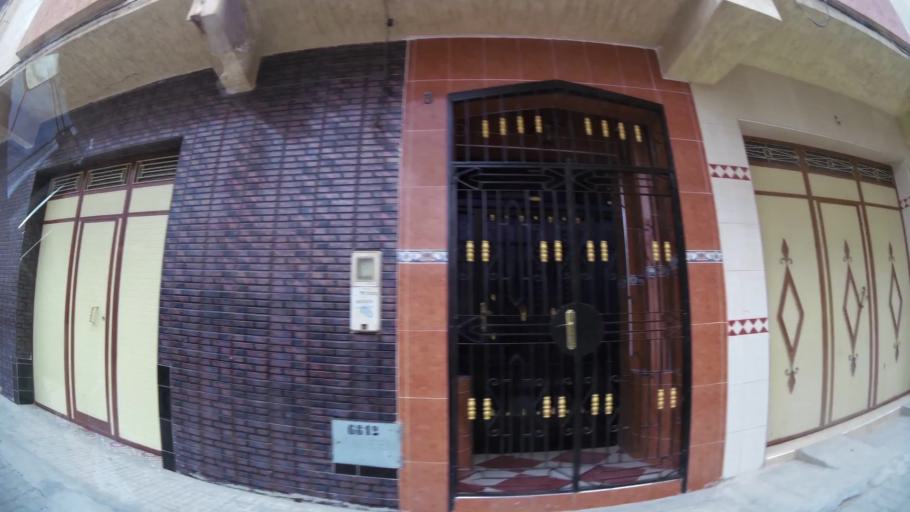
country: MA
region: Oriental
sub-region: Nador
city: Nador
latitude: 35.1687
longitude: -2.9377
